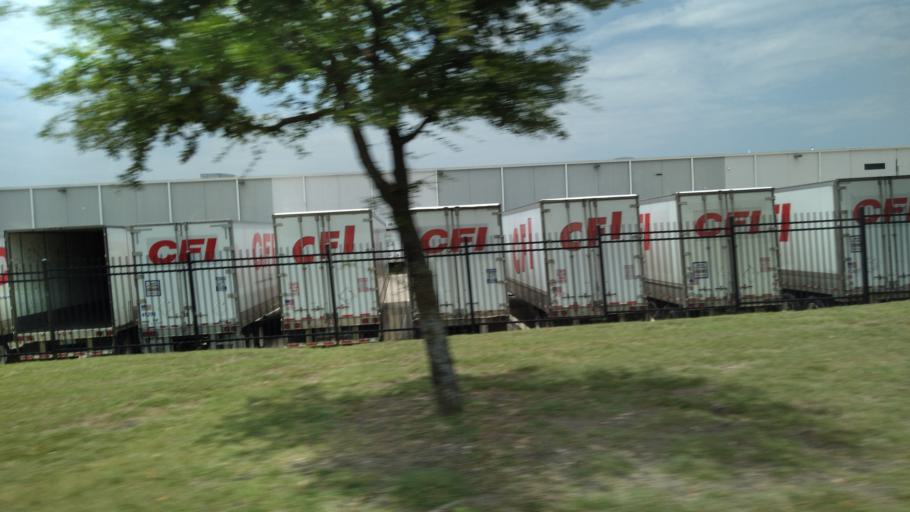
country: US
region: Texas
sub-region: McLennan County
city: Beverly Hills
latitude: 31.4872
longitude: -97.1586
